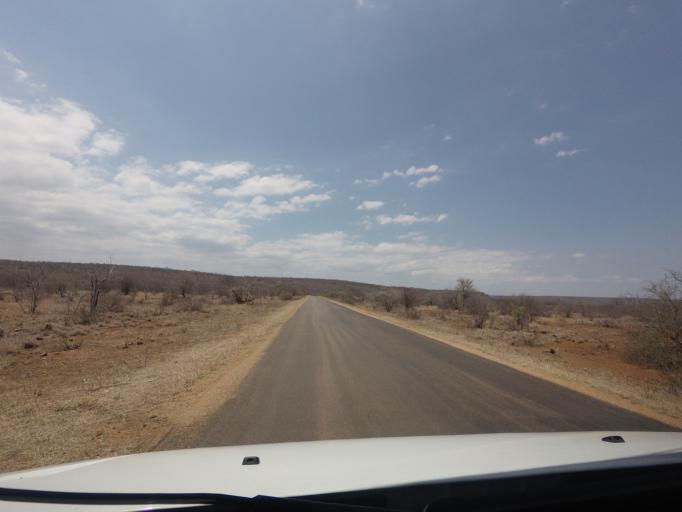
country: ZA
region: Limpopo
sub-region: Mopani District Municipality
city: Phalaborwa
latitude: -24.0029
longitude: 31.7147
